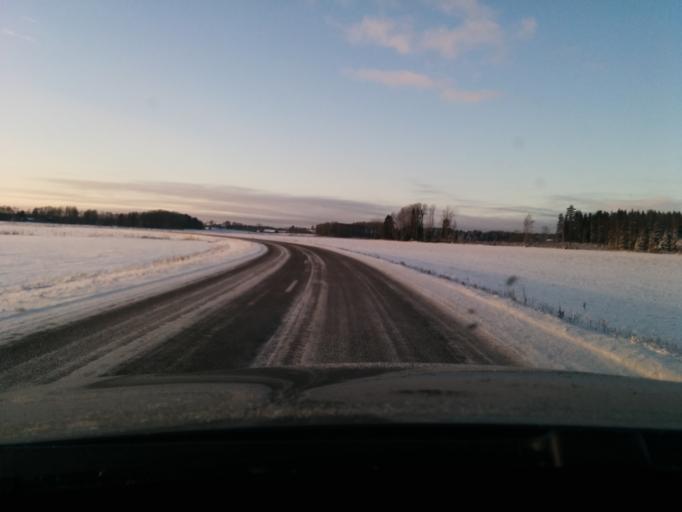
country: SE
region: Uppsala
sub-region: Tierps Kommun
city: Orbyhus
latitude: 60.1776
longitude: 17.6500
